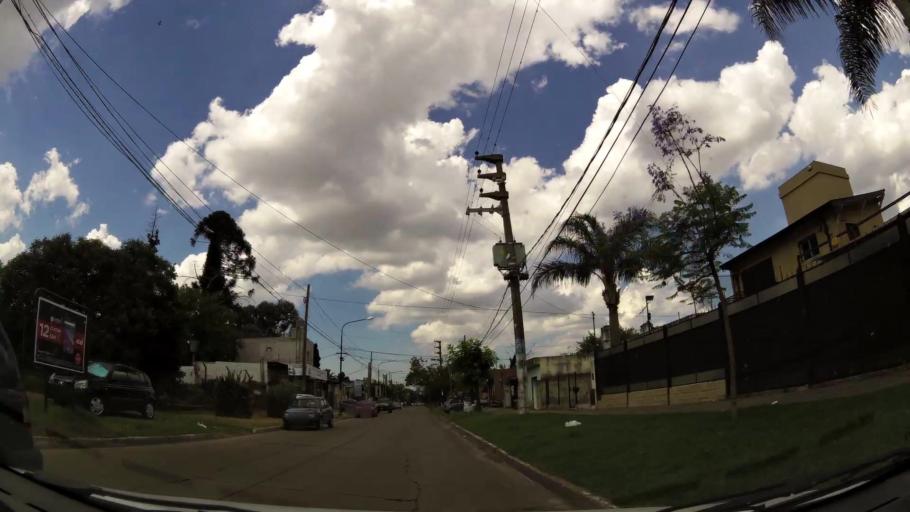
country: AR
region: Buenos Aires
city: Ituzaingo
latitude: -34.6513
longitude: -58.6742
